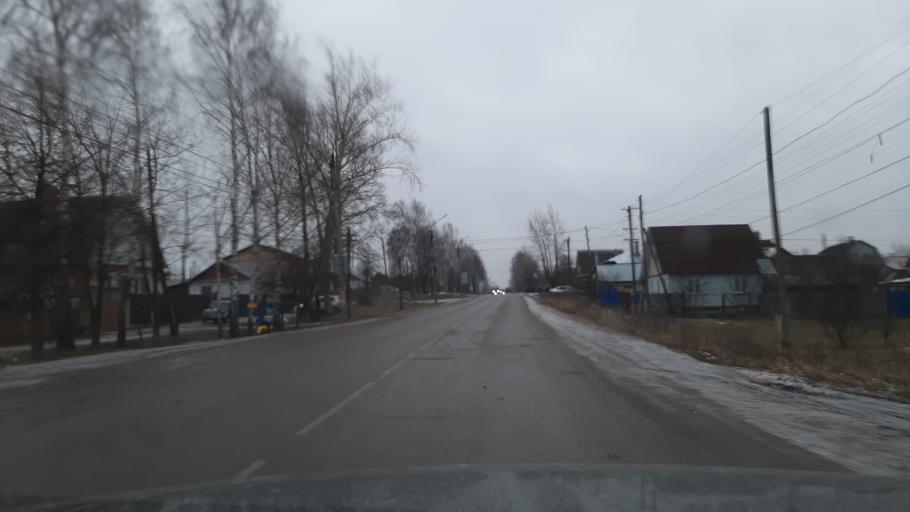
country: RU
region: Ivanovo
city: Shuya
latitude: 56.8740
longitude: 41.3518
